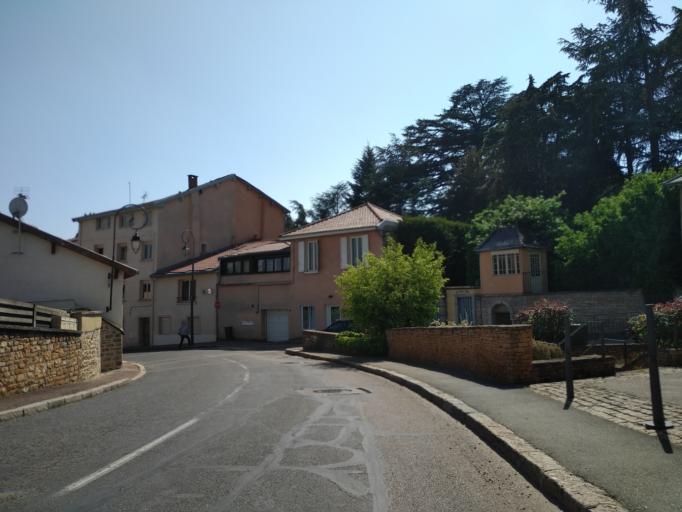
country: FR
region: Rhone-Alpes
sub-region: Departement du Rhone
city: Caluire-et-Cuire
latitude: 45.8131
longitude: 4.8181
